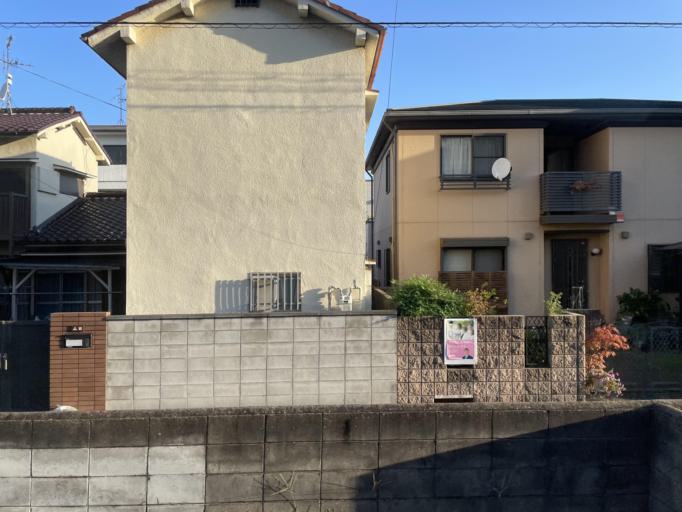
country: JP
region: Osaka
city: Matsubara
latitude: 34.5755
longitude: 135.5596
